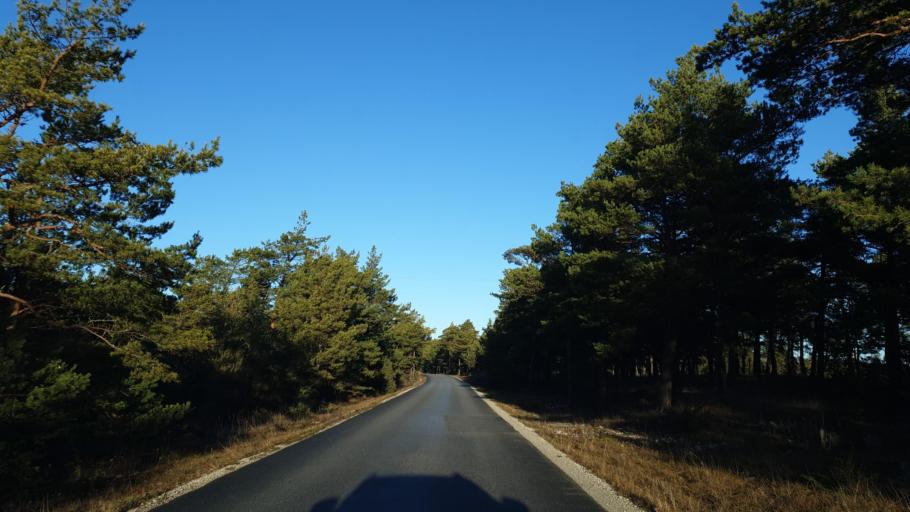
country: SE
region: Gotland
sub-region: Gotland
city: Slite
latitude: 57.9720
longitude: 19.1525
